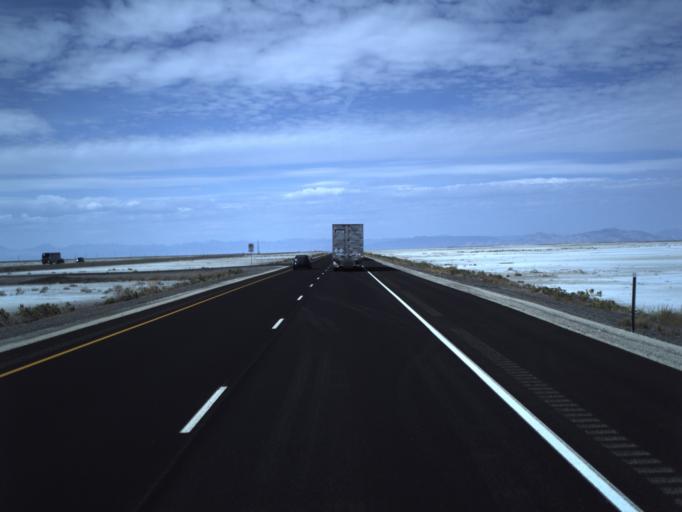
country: US
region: Utah
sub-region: Tooele County
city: Wendover
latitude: 40.7318
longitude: -113.4977
